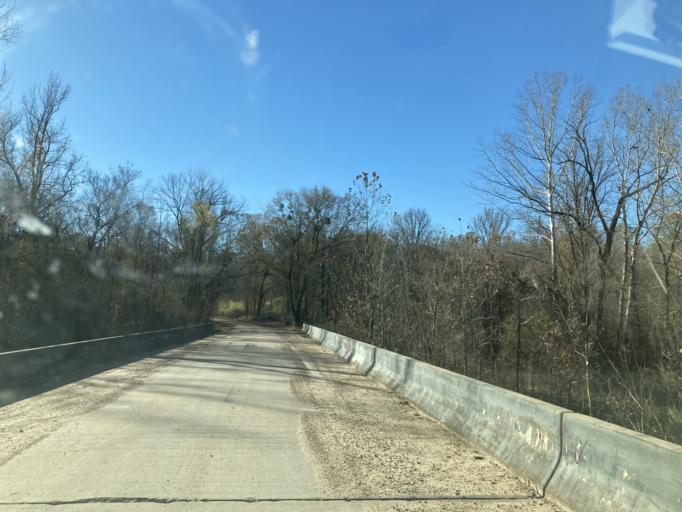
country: US
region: Mississippi
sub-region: Yazoo County
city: Yazoo City
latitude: 32.7118
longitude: -90.4160
